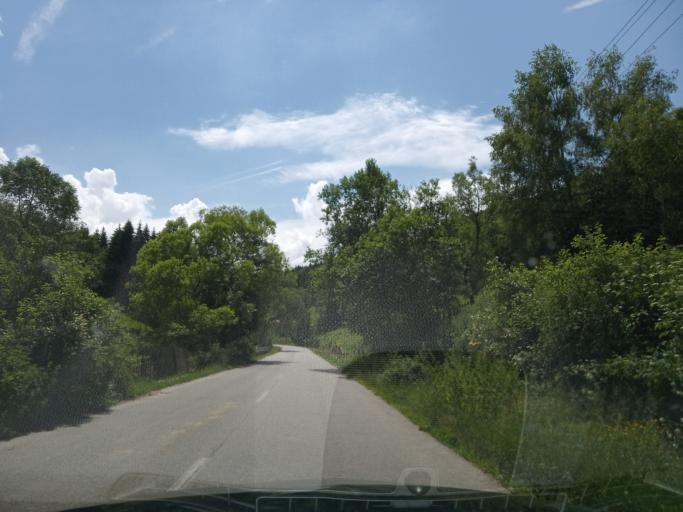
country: RO
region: Hunedoara
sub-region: Oras Petrila
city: Petrila
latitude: 45.4011
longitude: 23.4154
